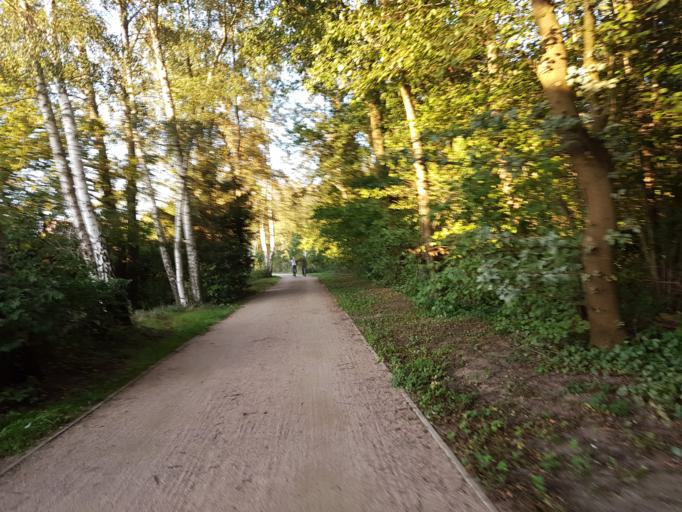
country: DE
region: Lower Saxony
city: Langenhagen
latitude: 52.4351
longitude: 9.7610
